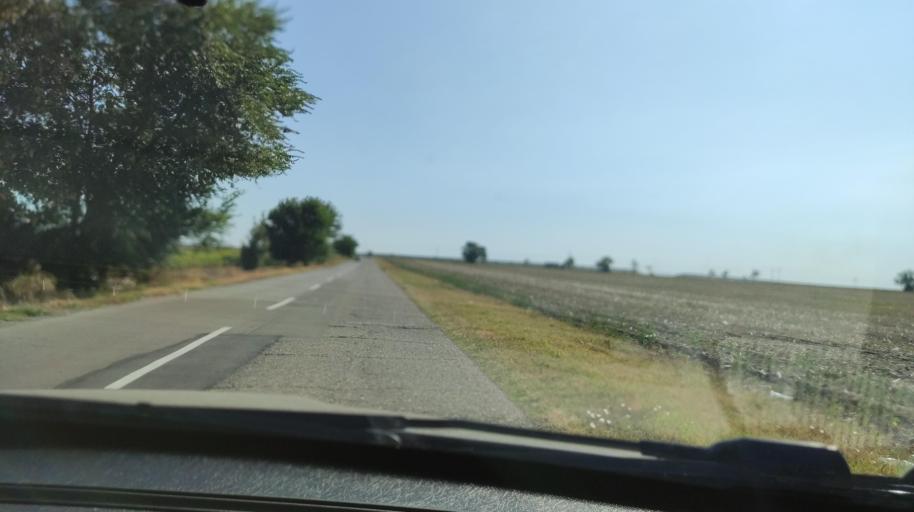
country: RS
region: Autonomna Pokrajina Vojvodina
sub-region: Severnobacki Okrug
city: Backa Topola
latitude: 45.8687
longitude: 19.6297
